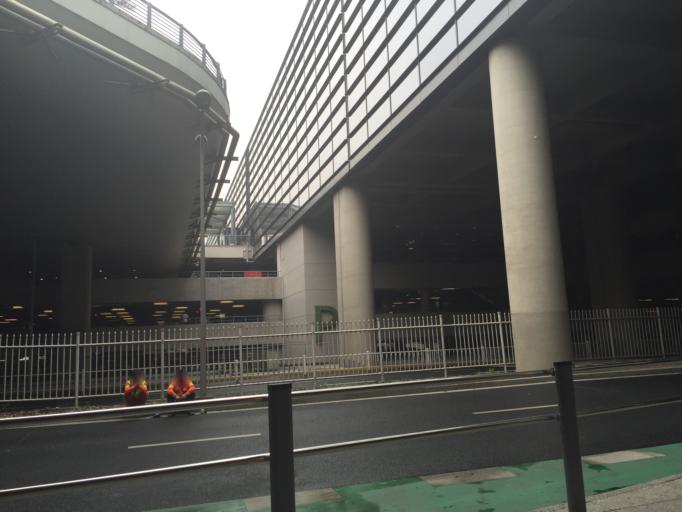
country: CN
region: Shanghai Shi
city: Huacao
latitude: 31.1956
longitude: 121.3227
